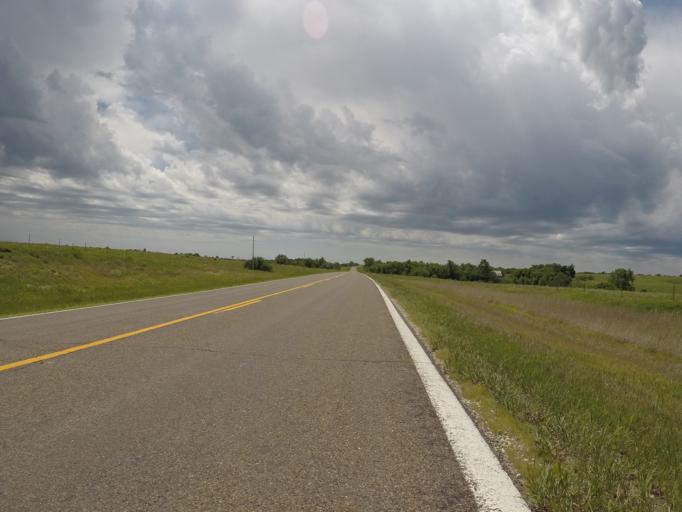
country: US
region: Kansas
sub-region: Wabaunsee County
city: Alma
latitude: 38.8653
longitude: -96.3725
